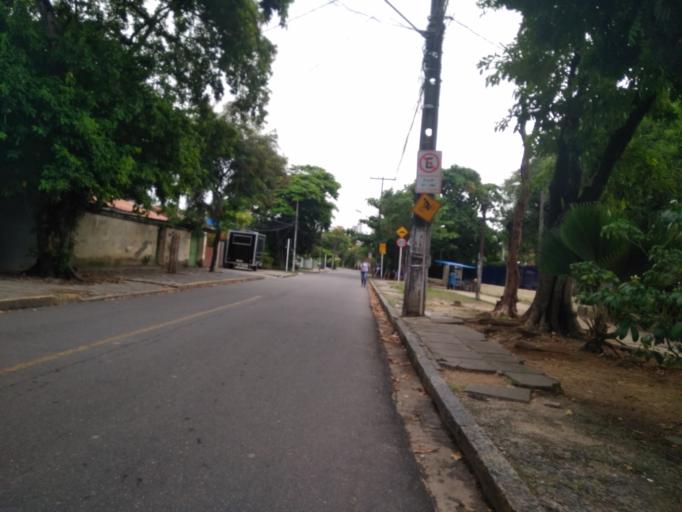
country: BR
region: Pernambuco
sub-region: Recife
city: Recife
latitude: -8.0327
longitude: -34.8866
